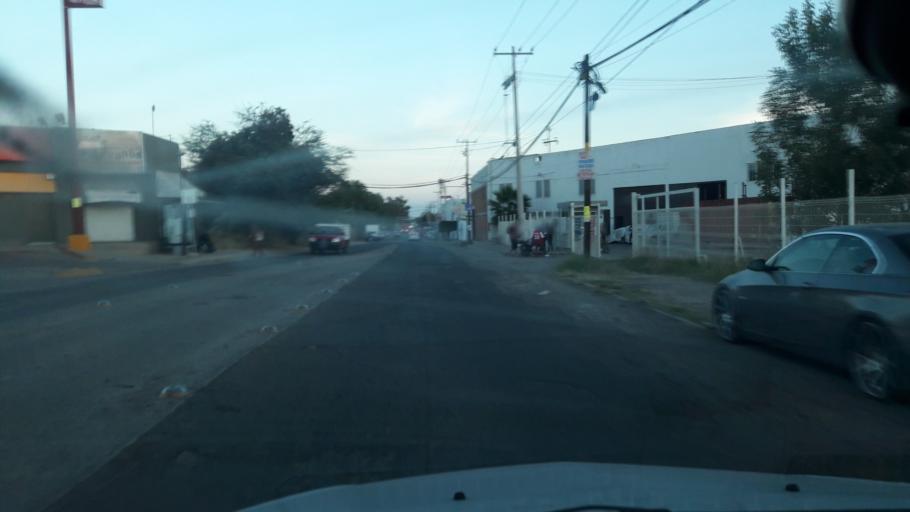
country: MX
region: Guanajuato
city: Leon
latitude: 21.1693
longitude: -101.6783
